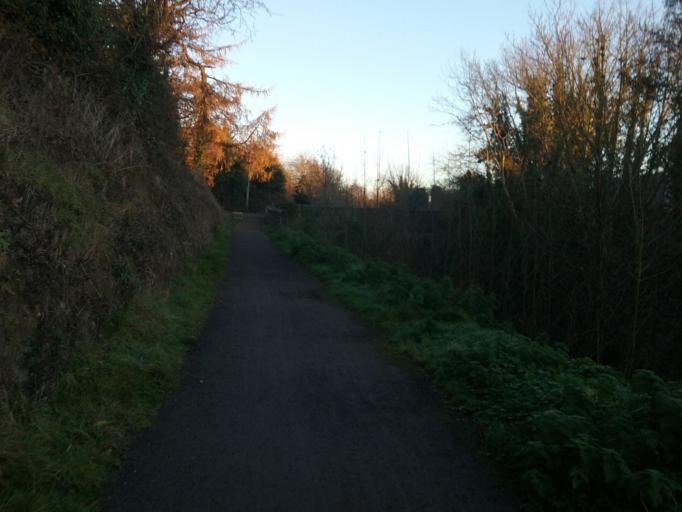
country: IE
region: Leinster
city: Hartstown
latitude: 53.3799
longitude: -6.4062
